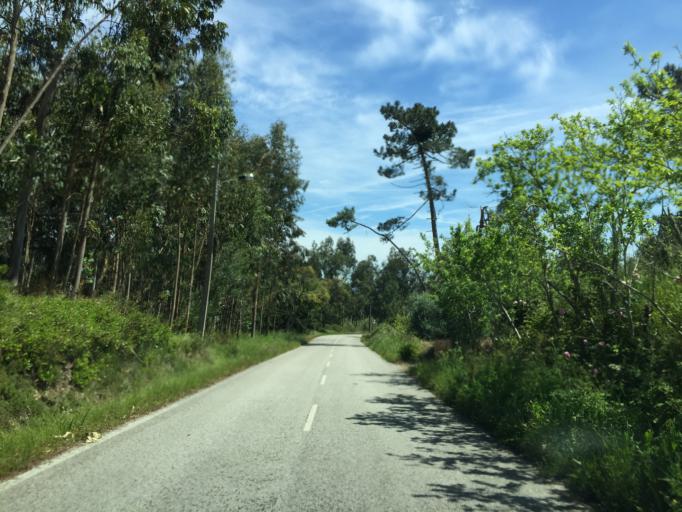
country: PT
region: Coimbra
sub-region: Figueira da Foz
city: Lavos
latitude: 40.0702
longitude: -8.7678
